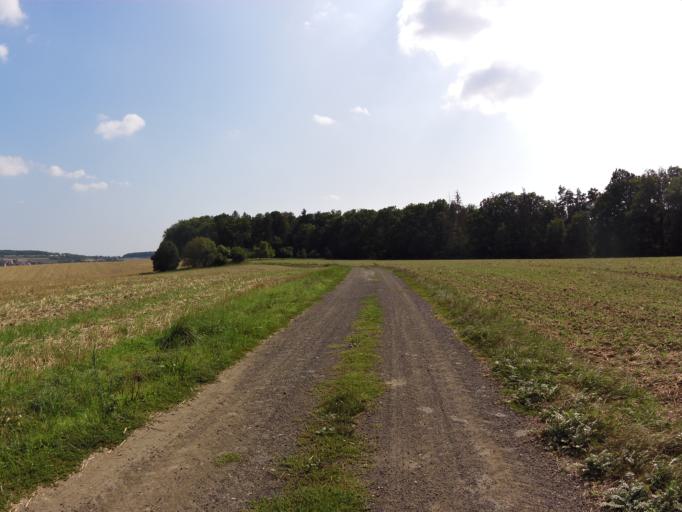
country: DE
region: Bavaria
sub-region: Regierungsbezirk Unterfranken
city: Kleinrinderfeld
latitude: 49.7079
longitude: 9.8246
